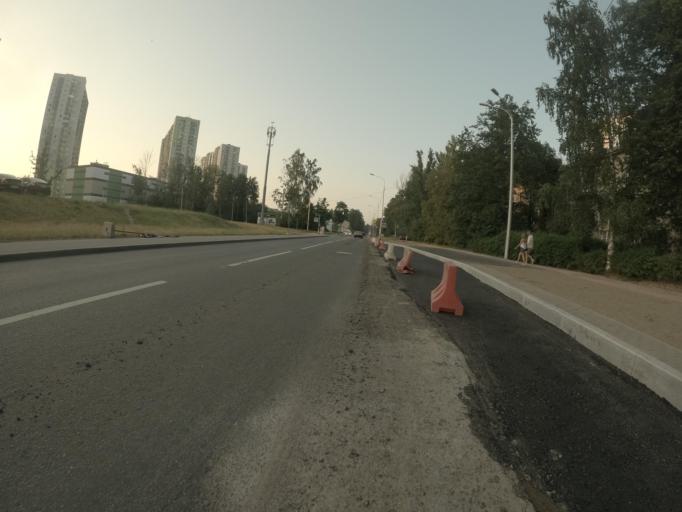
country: RU
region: Leningrad
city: Kalininskiy
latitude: 59.9831
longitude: 30.3875
